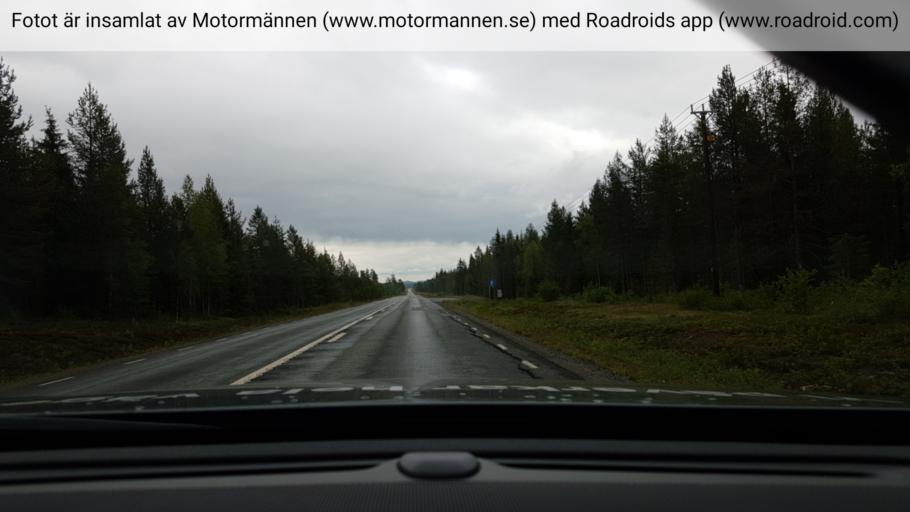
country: SE
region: Vaesterbotten
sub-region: Norsjo Kommun
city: Norsjoe
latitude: 65.2453
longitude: 19.7025
